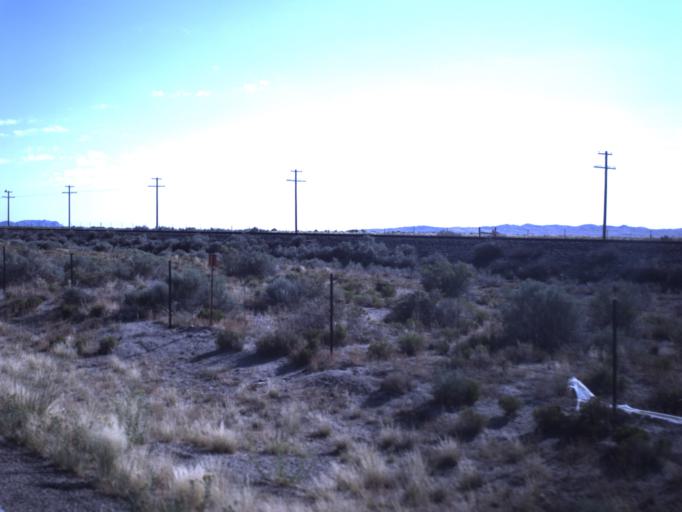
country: US
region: Utah
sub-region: Beaver County
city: Milford
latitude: 38.6576
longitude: -112.9818
